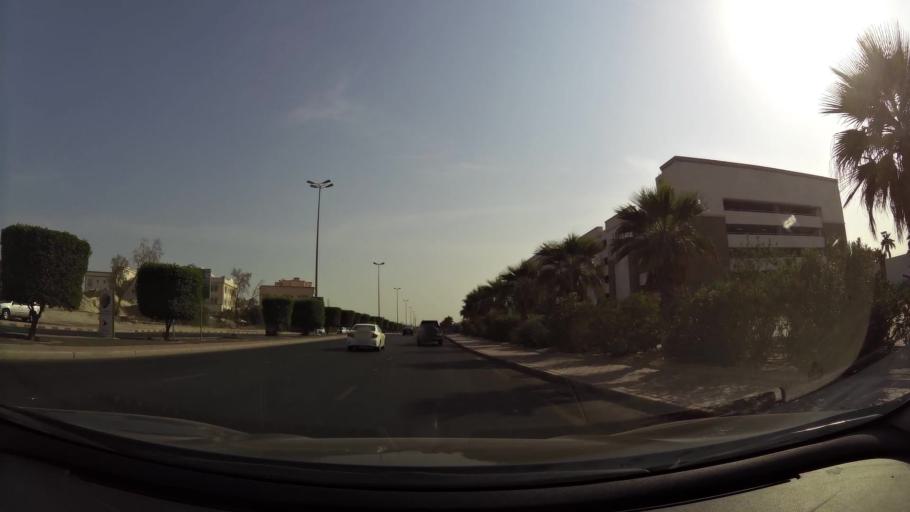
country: KW
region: Al Ahmadi
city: Al Fintas
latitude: 29.1673
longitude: 48.1011
